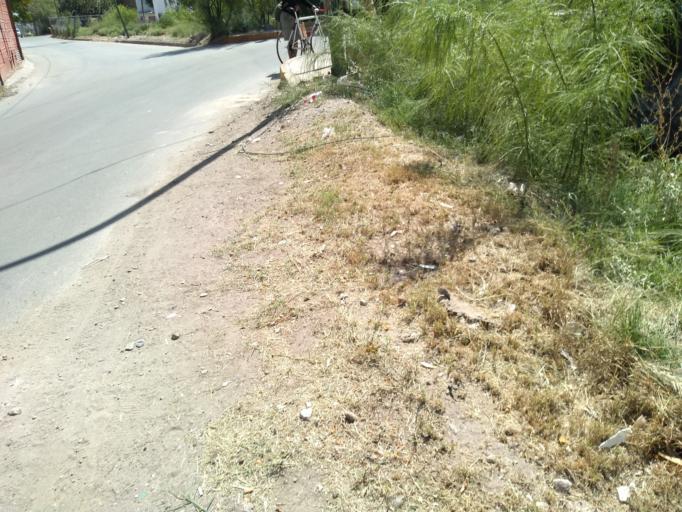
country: MX
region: Chihuahua
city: Ciudad Juarez
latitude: 31.7437
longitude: -106.4889
